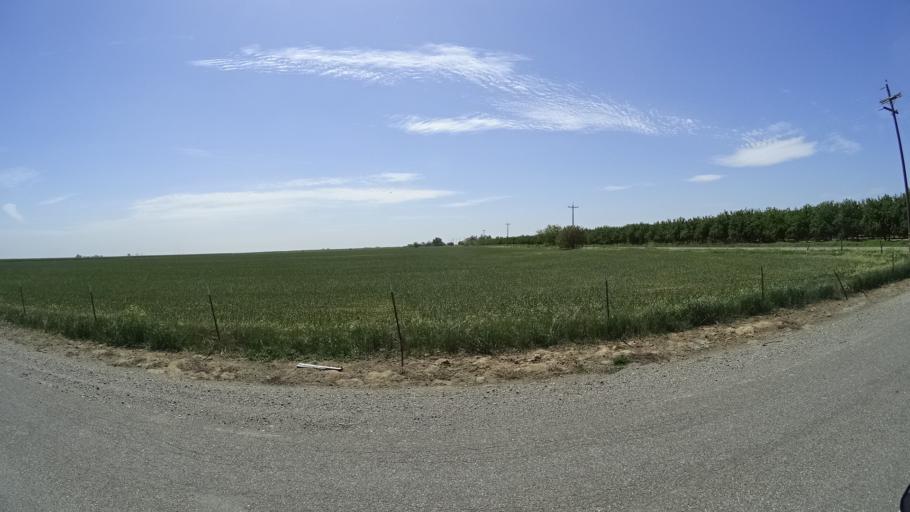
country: US
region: California
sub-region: Glenn County
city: Orland
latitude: 39.6530
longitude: -122.1591
